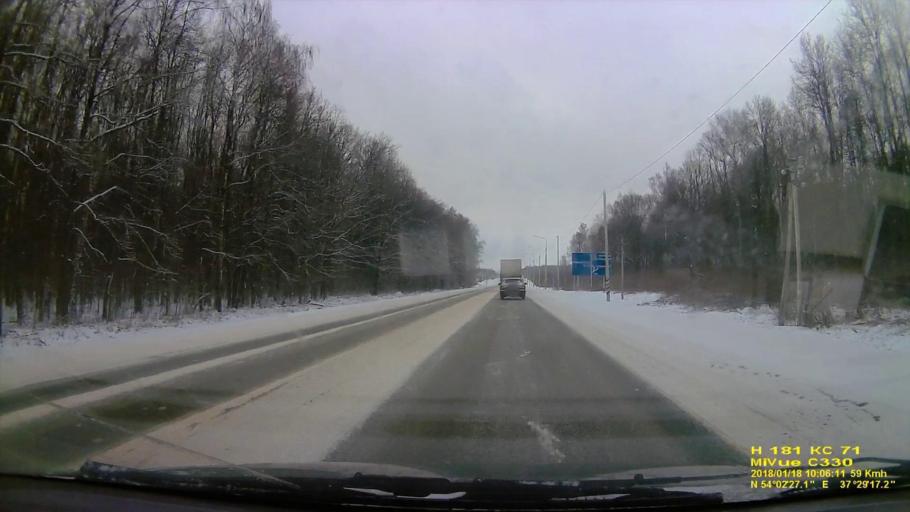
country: RU
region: Tula
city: Pervomayskiy
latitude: 54.0406
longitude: 37.4881
